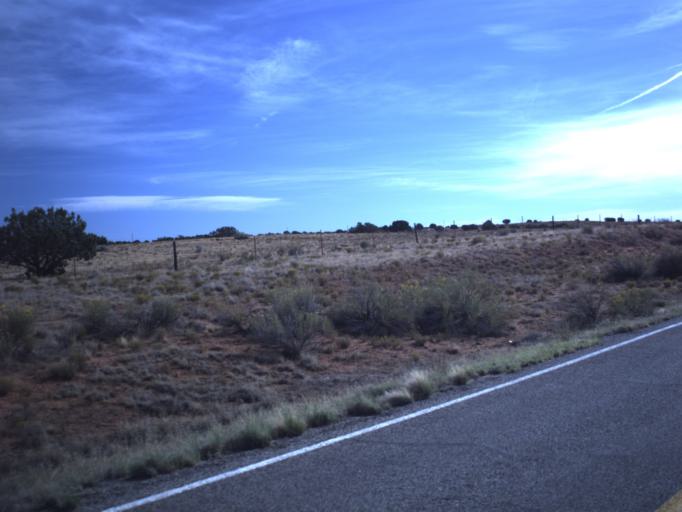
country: US
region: Utah
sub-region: San Juan County
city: Blanding
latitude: 37.4358
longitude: -109.3821
